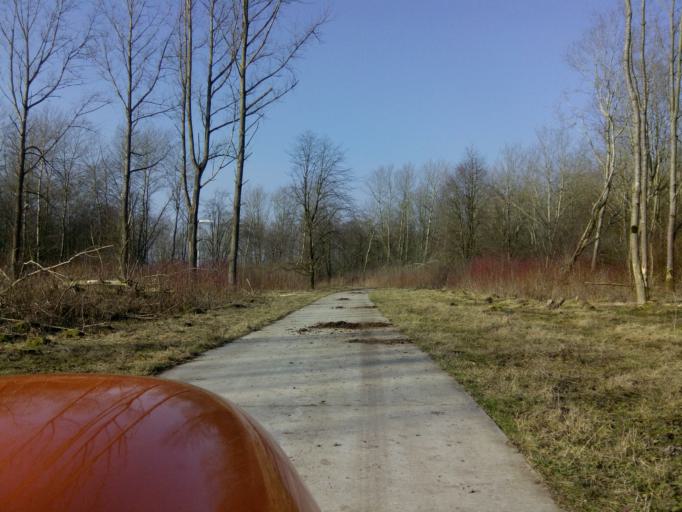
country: NL
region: Flevoland
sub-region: Gemeente Zeewolde
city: Zeewolde
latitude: 52.3103
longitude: 5.4526
